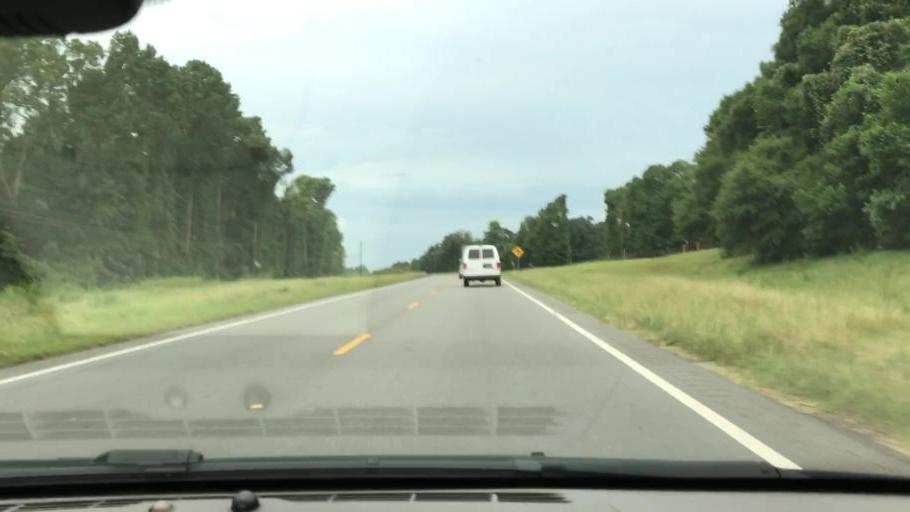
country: US
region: Alabama
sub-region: Houston County
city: Webb
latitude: 31.2921
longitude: -85.1278
